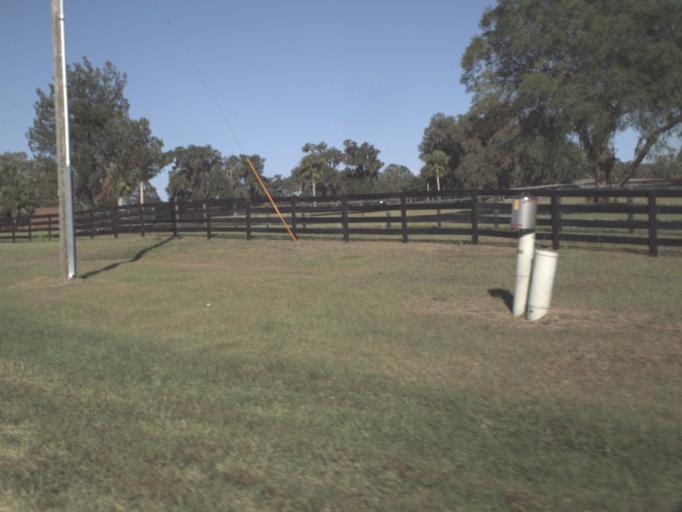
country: US
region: Florida
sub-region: Marion County
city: Dunnellon
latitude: 29.1605
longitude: -82.3477
